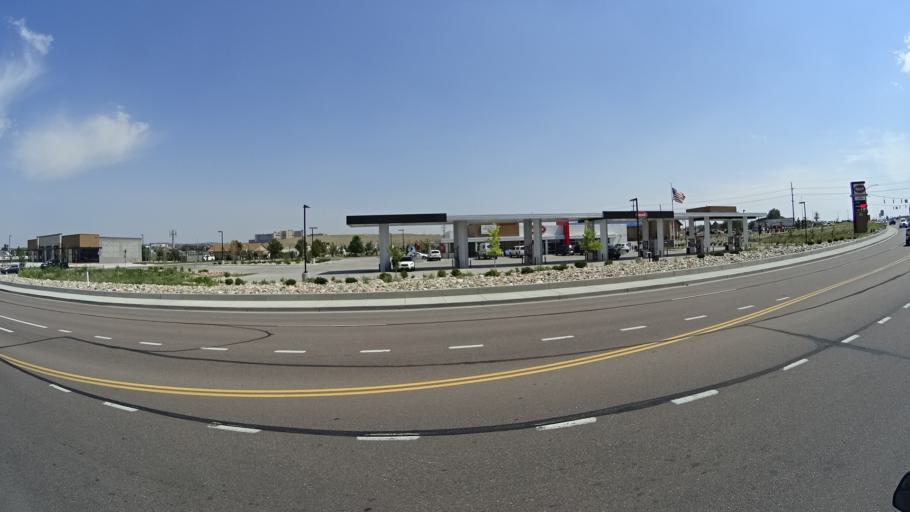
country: US
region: Colorado
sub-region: El Paso County
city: Cimarron Hills
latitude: 38.9264
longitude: -104.7217
